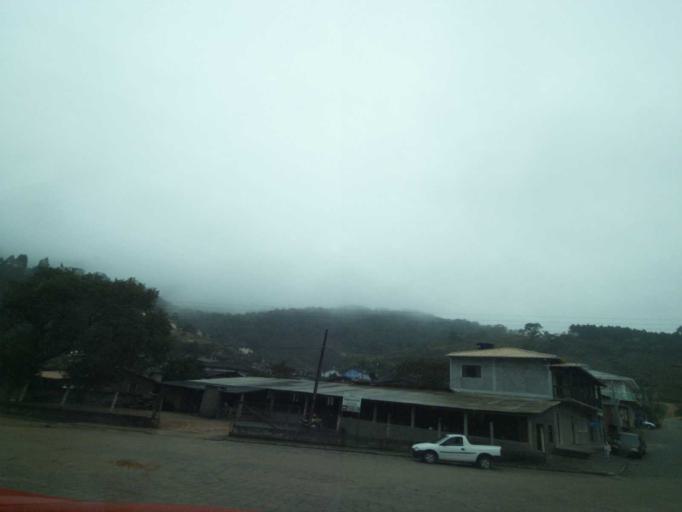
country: BR
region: Santa Catarina
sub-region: Anitapolis
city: Anitapolis
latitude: -27.9106
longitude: -49.1327
